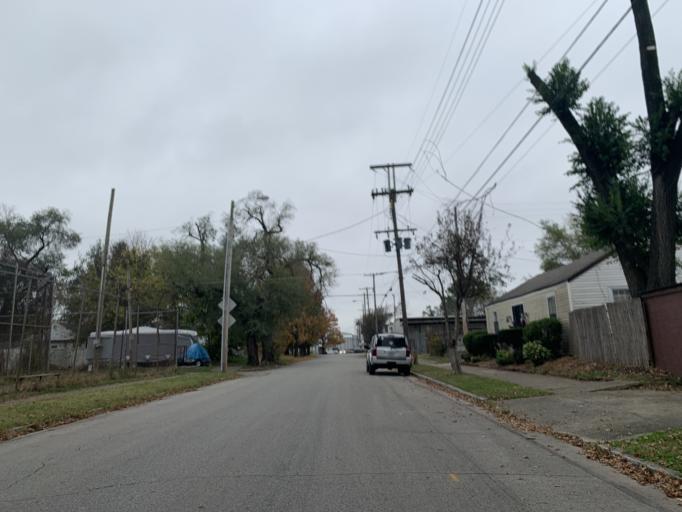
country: US
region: Indiana
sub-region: Floyd County
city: New Albany
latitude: 38.2626
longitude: -85.8005
